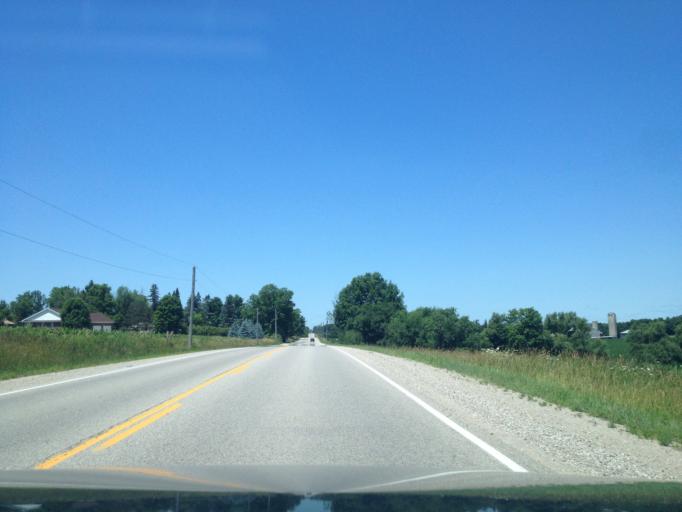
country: CA
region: Ontario
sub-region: Wellington County
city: Guelph
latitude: 43.6233
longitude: -80.2250
